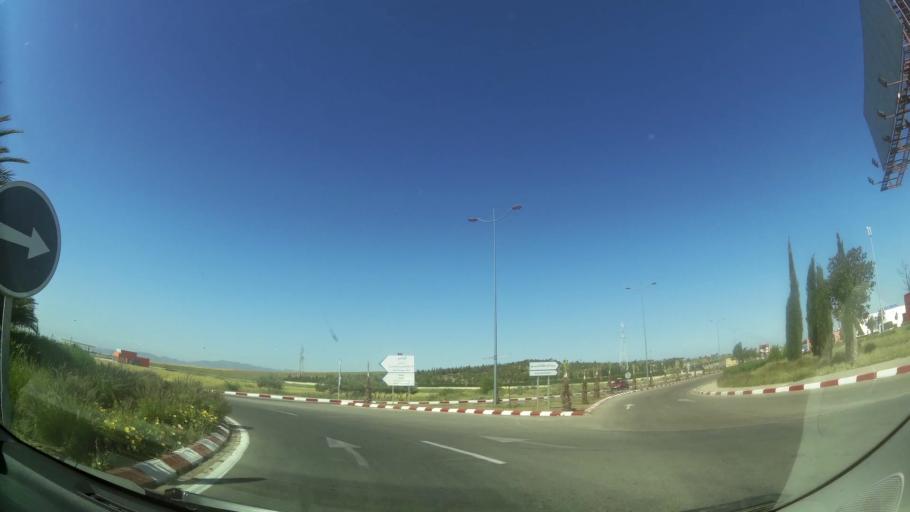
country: MA
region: Oriental
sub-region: Oujda-Angad
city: Oujda
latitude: 34.7373
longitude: -1.9291
